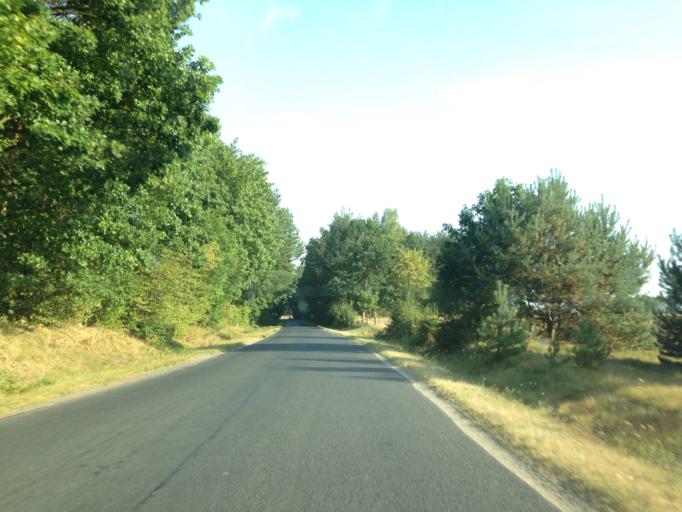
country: PL
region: Warmian-Masurian Voivodeship
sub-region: Powiat nowomiejski
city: Biskupiec
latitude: 53.3960
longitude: 19.3603
